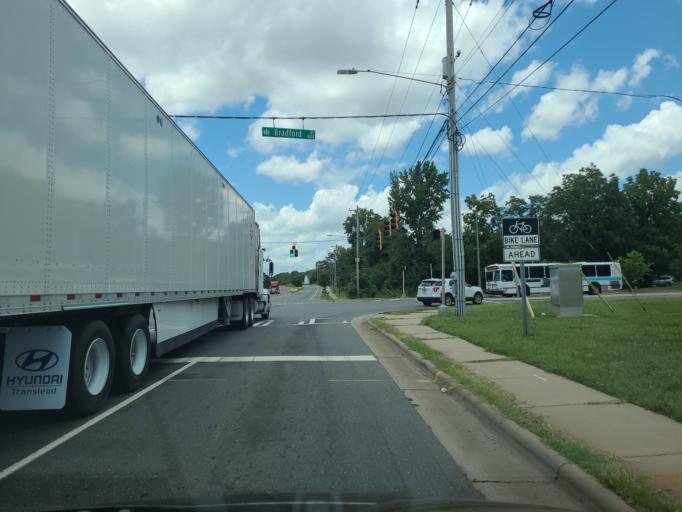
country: US
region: North Carolina
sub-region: Mecklenburg County
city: Charlotte
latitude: 35.2503
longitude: -80.8986
